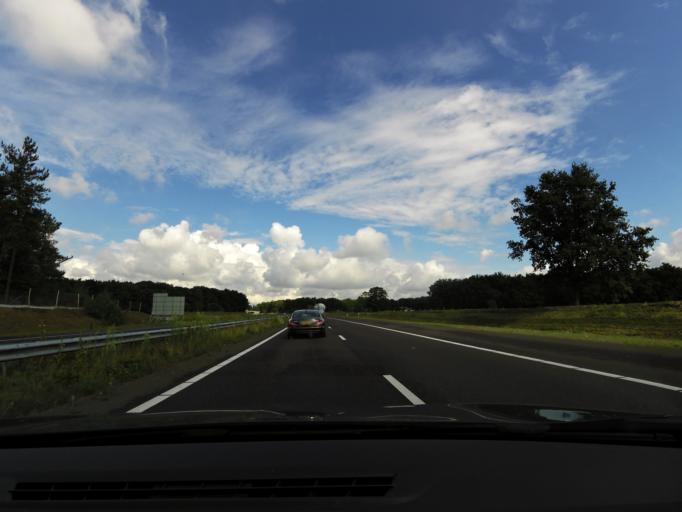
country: NL
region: North Brabant
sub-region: Gemeente Bergen op Zoom
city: Bergen op Zoom
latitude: 51.5201
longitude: 4.3113
